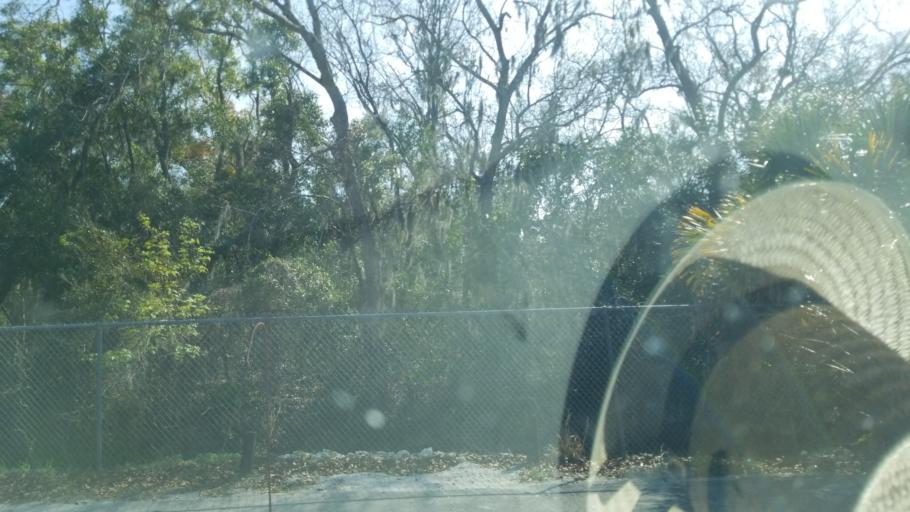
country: US
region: Florida
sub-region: Sarasota County
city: Southgate
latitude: 27.3194
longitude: -82.5038
